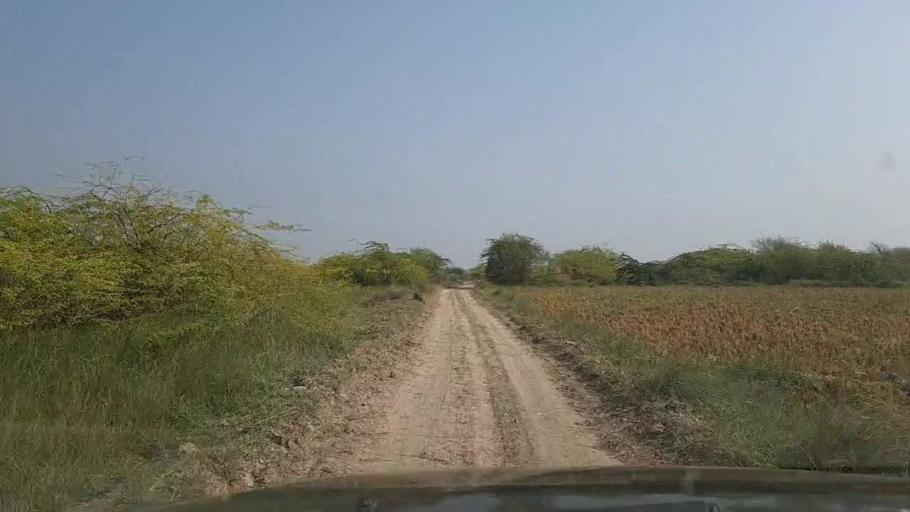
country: PK
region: Sindh
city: Mirpur Batoro
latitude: 24.6782
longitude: 68.2425
